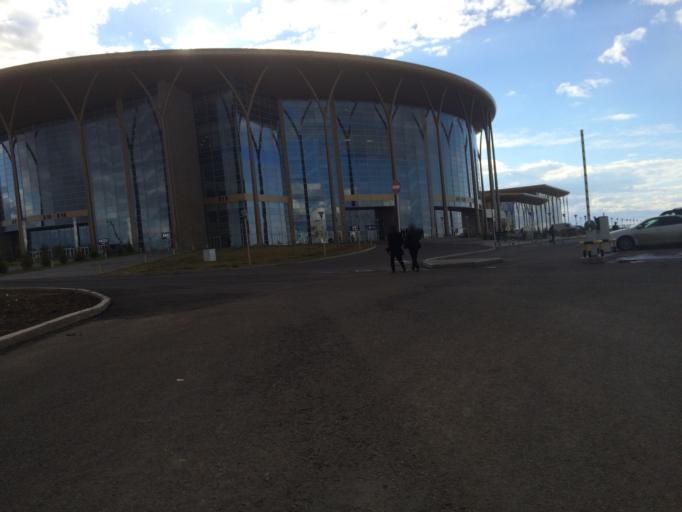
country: KZ
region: Astana Qalasy
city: Astana
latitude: 51.1099
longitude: 71.3979
